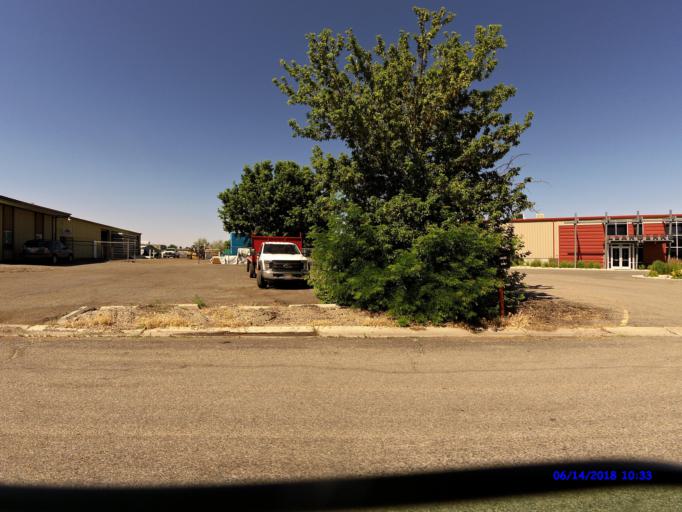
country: US
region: Utah
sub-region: Weber County
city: Marriott-Slaterville
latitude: 41.2153
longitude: -112.0149
